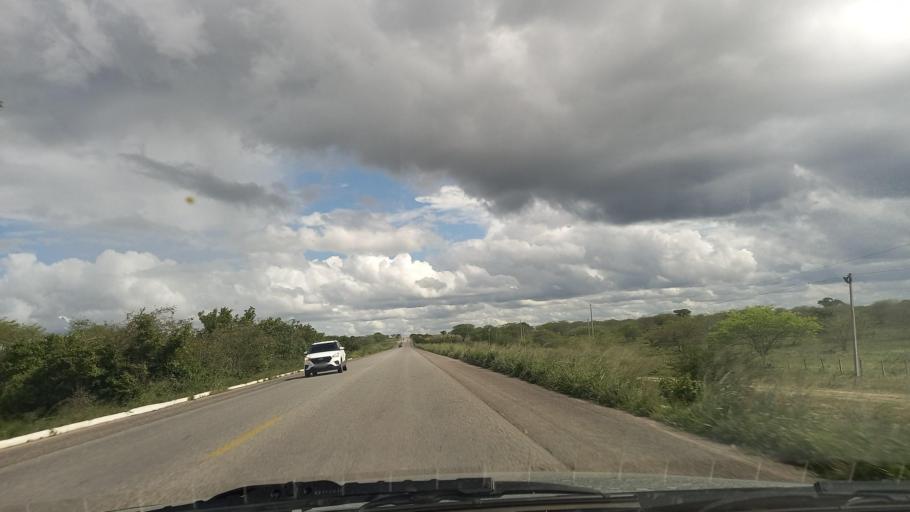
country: BR
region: Pernambuco
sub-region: Cachoeirinha
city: Cachoeirinha
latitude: -8.5126
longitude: -36.2531
